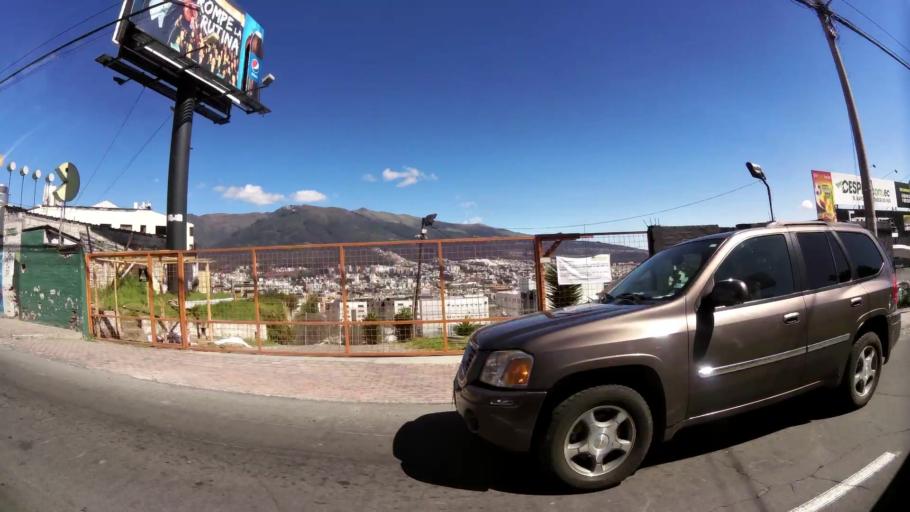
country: EC
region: Pichincha
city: Quito
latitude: -0.1709
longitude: -78.4705
